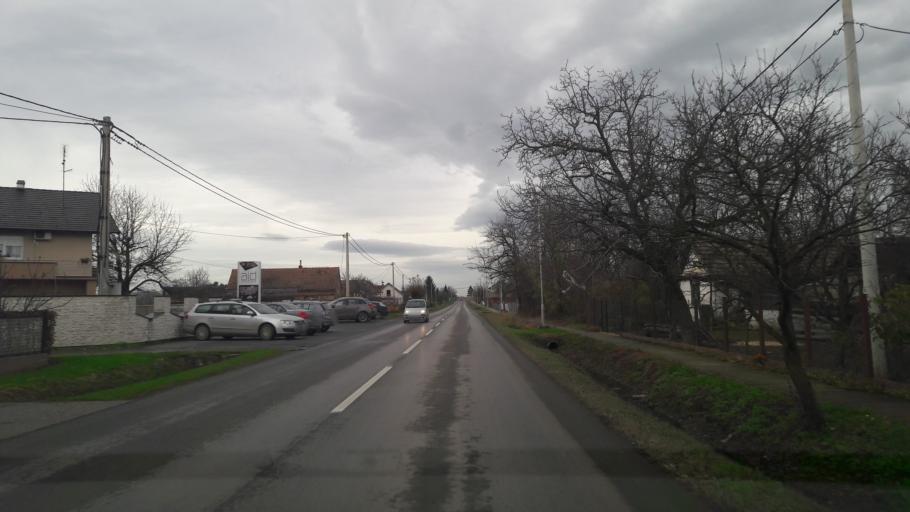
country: HR
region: Osjecko-Baranjska
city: Velimirovac
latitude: 45.5362
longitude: 18.0736
